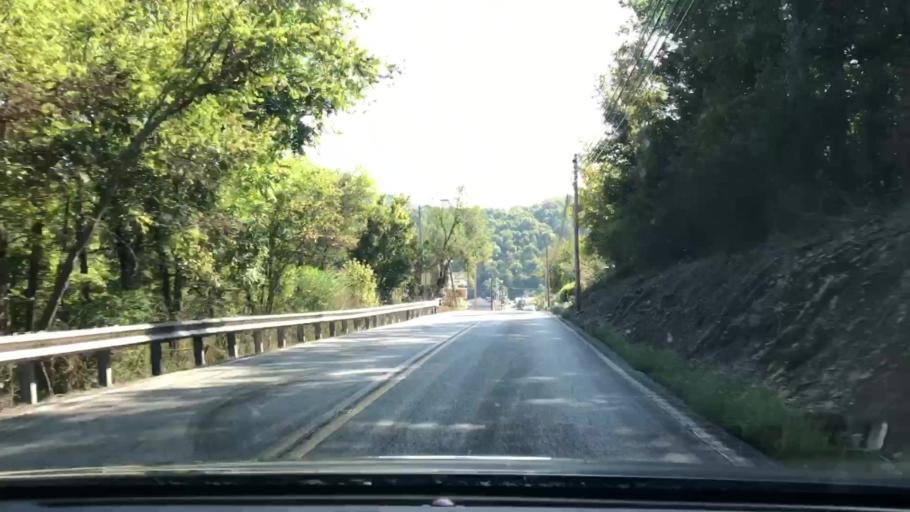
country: US
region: Tennessee
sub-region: Jackson County
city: Gainesboro
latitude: 36.3554
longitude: -85.6624
